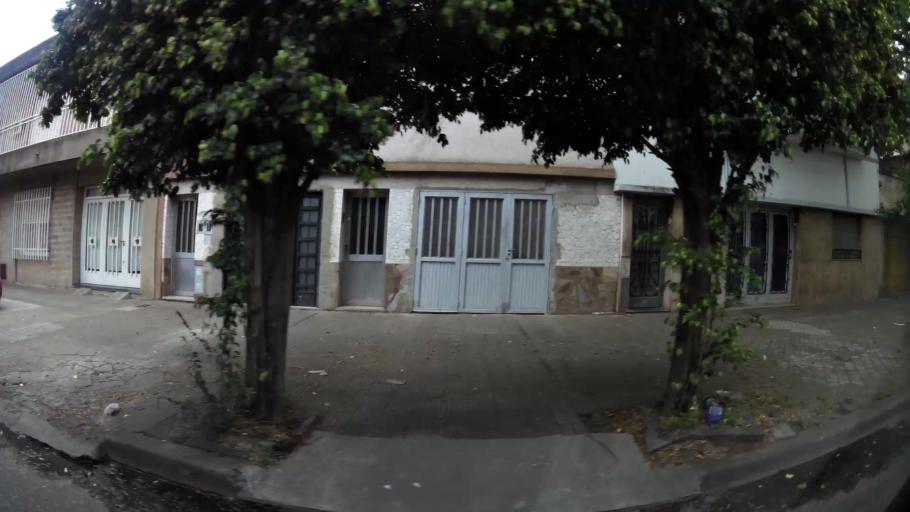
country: AR
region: Santa Fe
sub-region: Departamento de Rosario
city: Rosario
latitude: -32.9794
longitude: -60.6361
